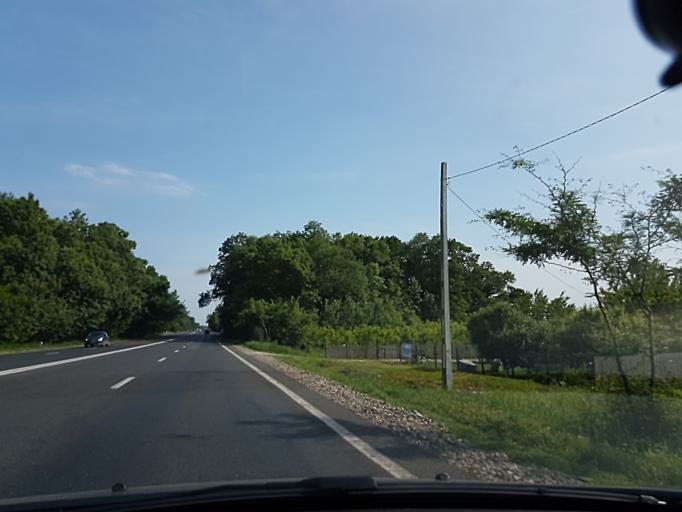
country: RO
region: Prahova
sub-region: Comuna Gorgota
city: Potigrafu
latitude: 44.7683
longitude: 26.1027
